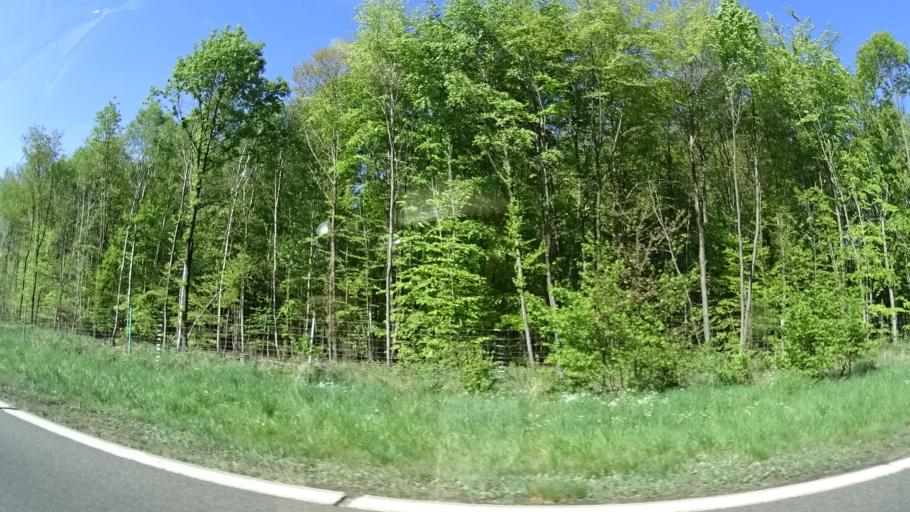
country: DE
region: Baden-Wuerttemberg
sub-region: Regierungsbezirk Stuttgart
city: Sindelfingen
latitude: 48.7258
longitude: 9.0642
